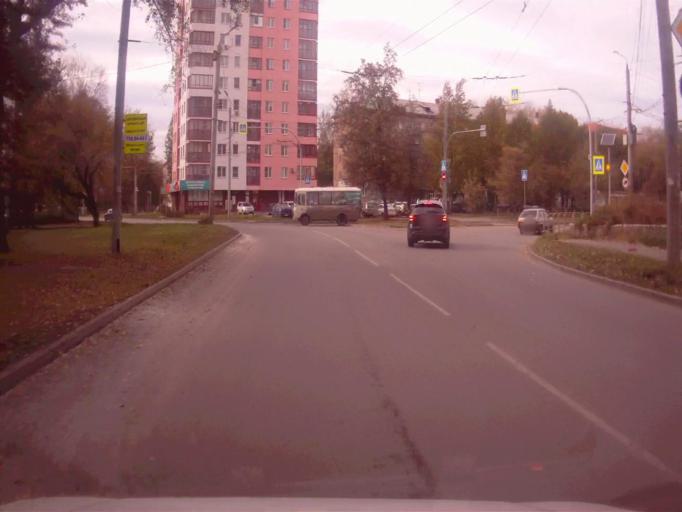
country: RU
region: Chelyabinsk
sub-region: Gorod Chelyabinsk
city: Chelyabinsk
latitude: 55.1169
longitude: 61.4369
